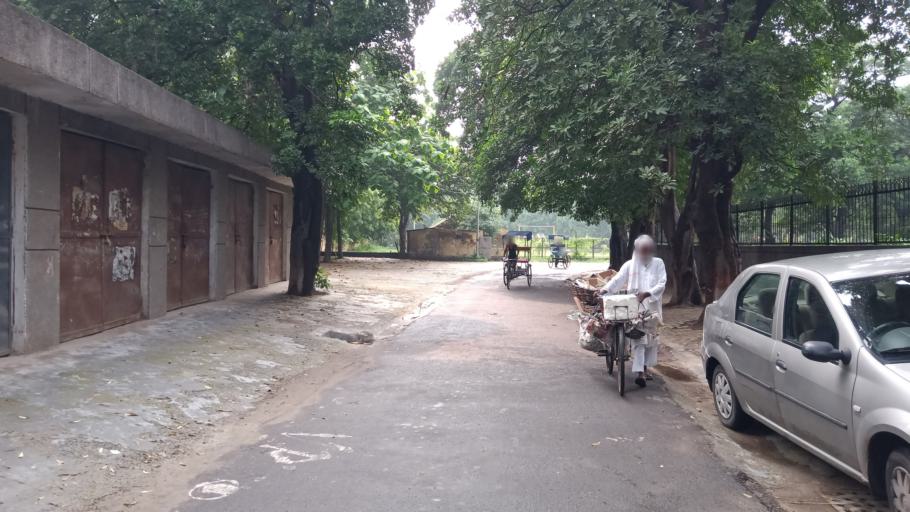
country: IN
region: NCT
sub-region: New Delhi
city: New Delhi
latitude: 28.5759
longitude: 77.2488
